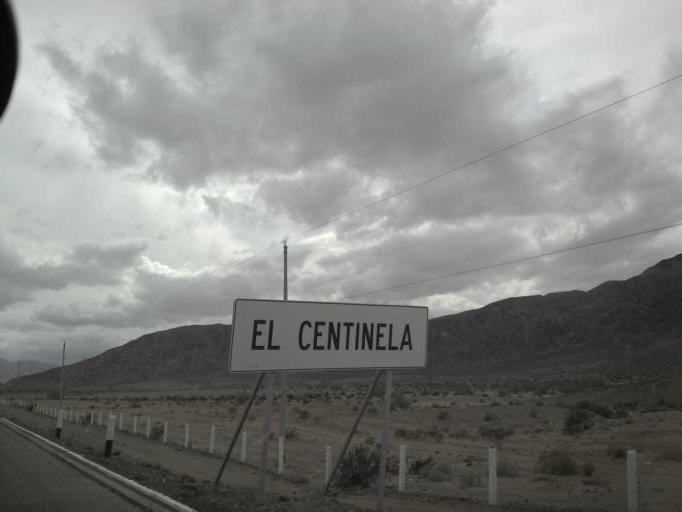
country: MX
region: Baja California
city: Progreso
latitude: 32.5895
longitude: -115.6997
